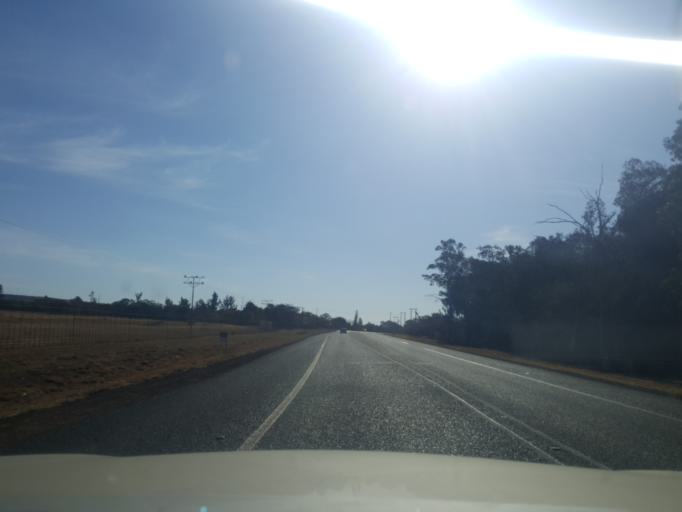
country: ZA
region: North-West
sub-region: Ngaka Modiri Molema District Municipality
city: Zeerust
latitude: -25.5593
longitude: 26.2207
